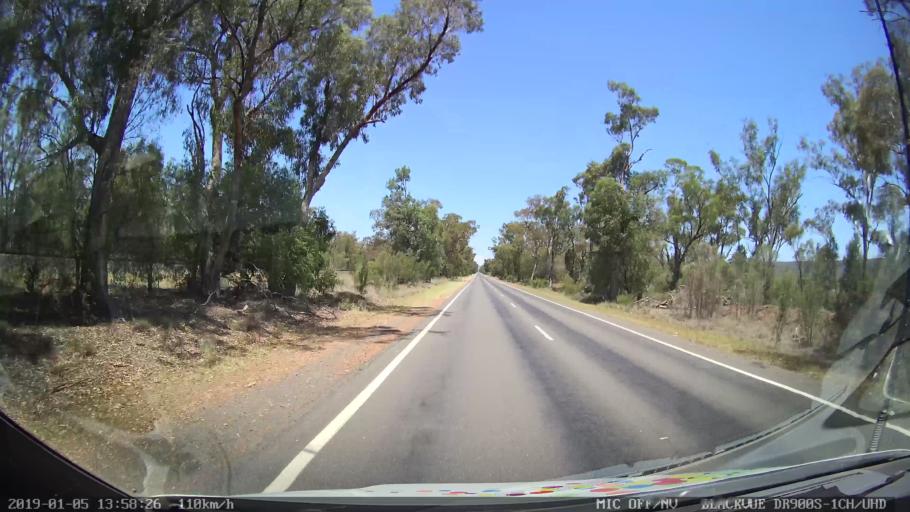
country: AU
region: New South Wales
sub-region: Gunnedah
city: Gunnedah
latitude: -31.1389
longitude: 150.2857
